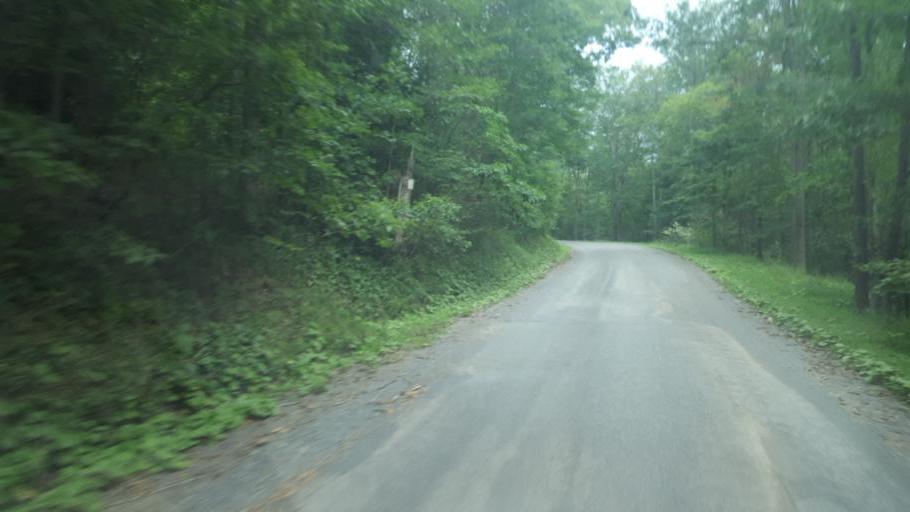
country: US
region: Pennsylvania
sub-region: Clarion County
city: Clarion
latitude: 41.2219
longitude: -79.4127
